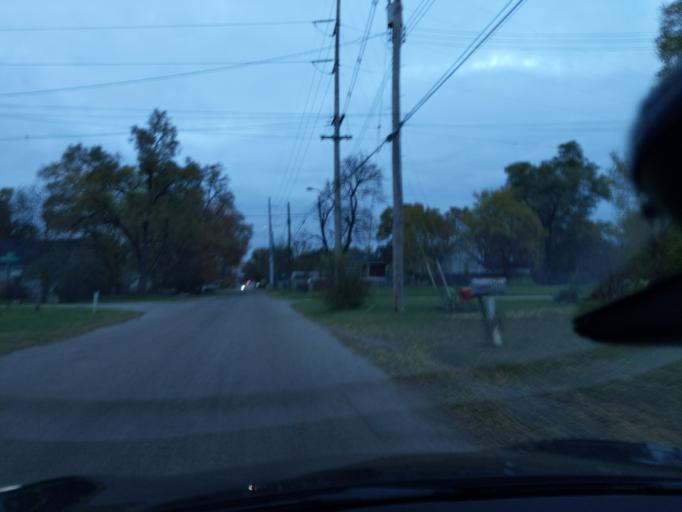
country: US
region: Michigan
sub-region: Ingham County
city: East Lansing
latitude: 42.7283
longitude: -84.5125
